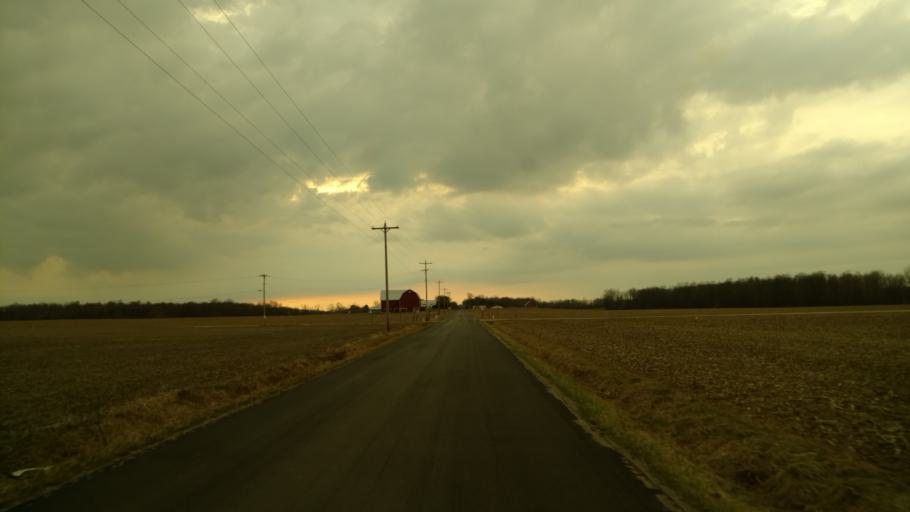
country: US
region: Ohio
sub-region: Richland County
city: Lexington
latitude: 40.6238
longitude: -82.7075
